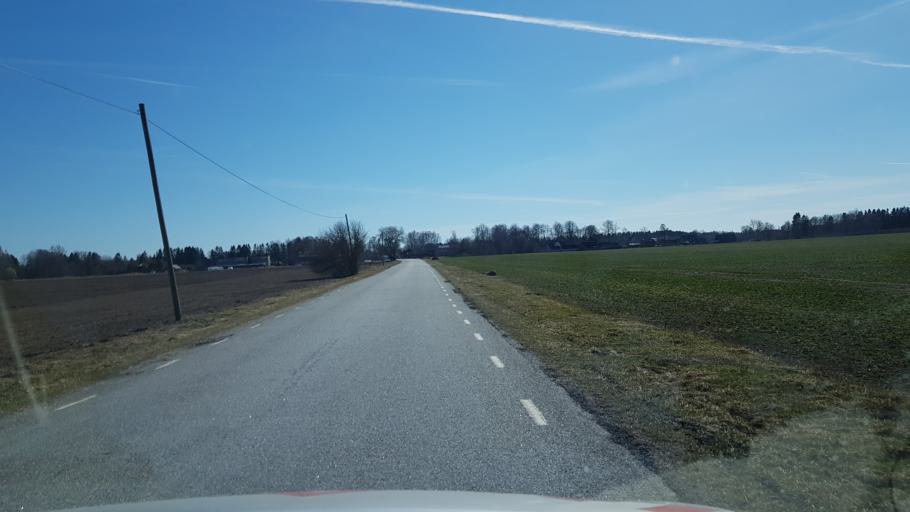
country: EE
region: Laeaene-Virumaa
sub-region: Viru-Nigula vald
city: Kunda
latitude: 59.3508
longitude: 26.6760
